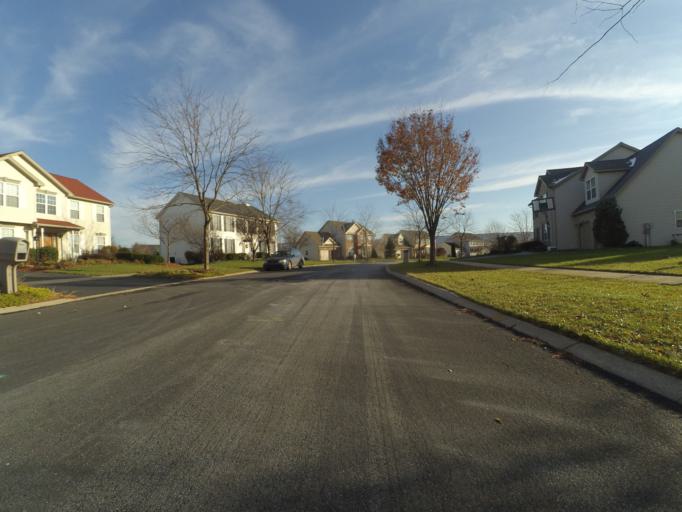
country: US
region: Pennsylvania
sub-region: Centre County
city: Pine Grove Mills
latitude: 40.7664
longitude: -77.8914
